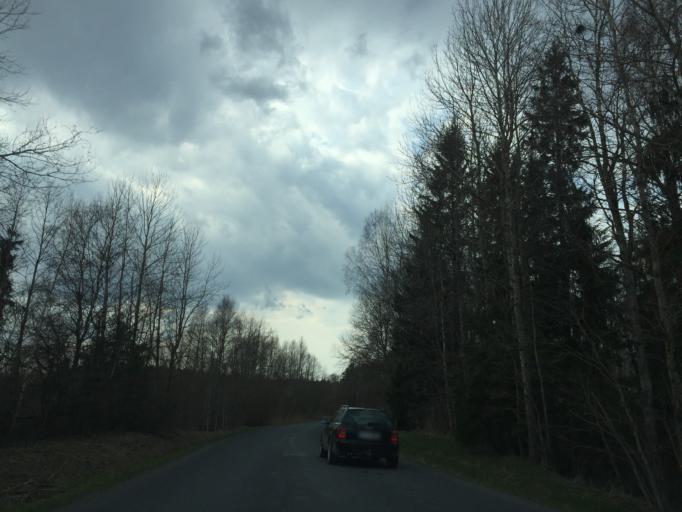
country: RU
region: Pskov
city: Pechory
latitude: 57.7378
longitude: 27.3174
